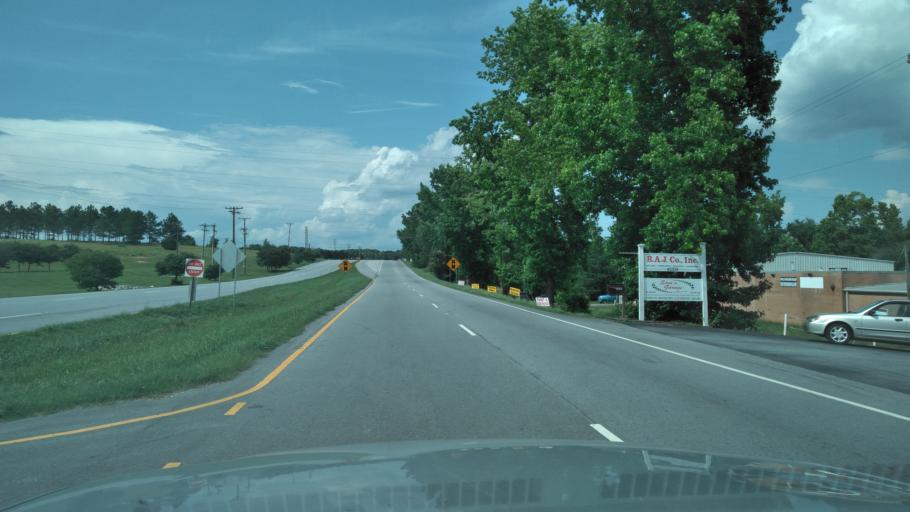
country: US
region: South Carolina
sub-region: Spartanburg County
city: Roebuck
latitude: 34.8493
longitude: -81.9671
